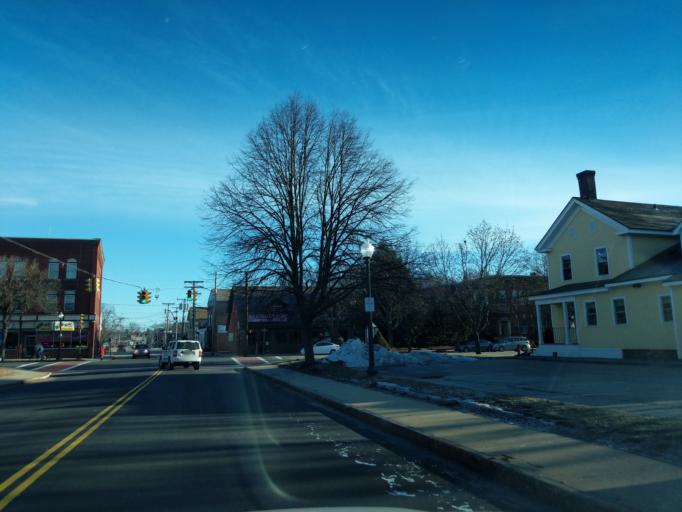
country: US
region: New Hampshire
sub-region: Strafford County
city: Rochester
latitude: 43.3028
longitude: -70.9754
